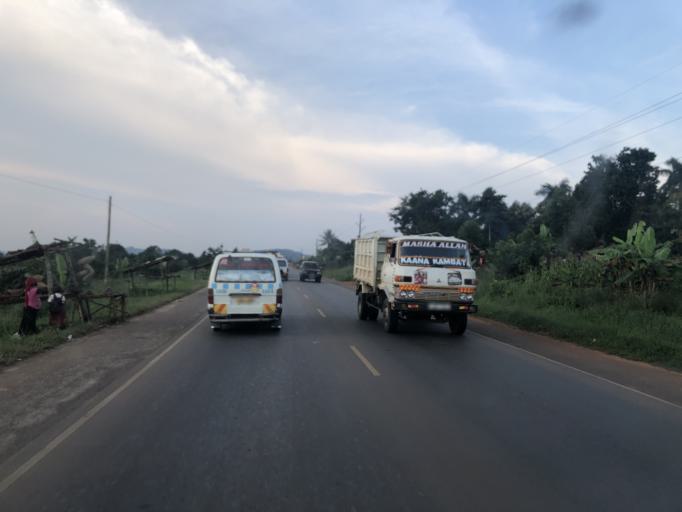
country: UG
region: Central Region
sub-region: Mpigi District
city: Mpigi
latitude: 0.2321
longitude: 32.3460
